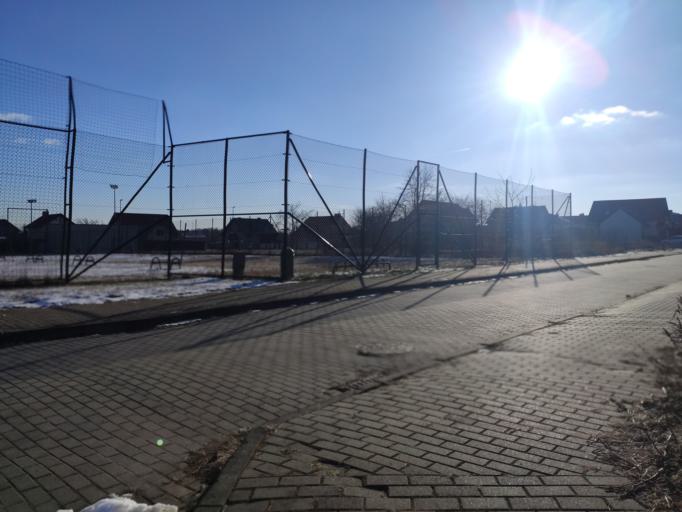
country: PL
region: Lublin Voivodeship
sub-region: Powiat lubartowski
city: Kock
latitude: 51.6421
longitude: 22.4362
